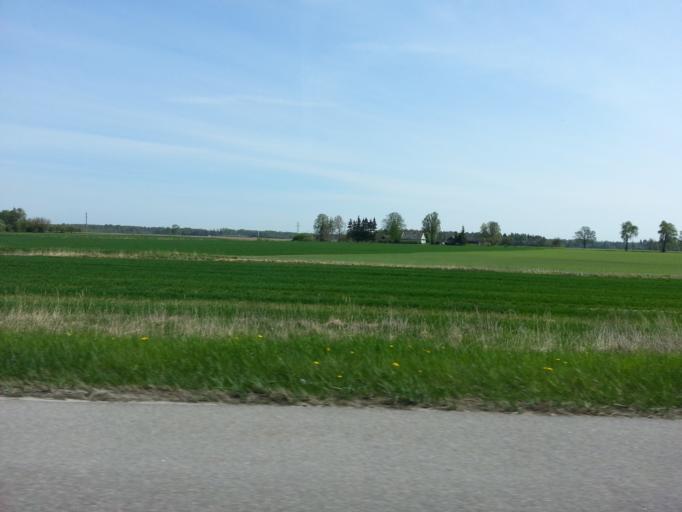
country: LT
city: Ramygala
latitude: 55.5438
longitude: 24.5317
